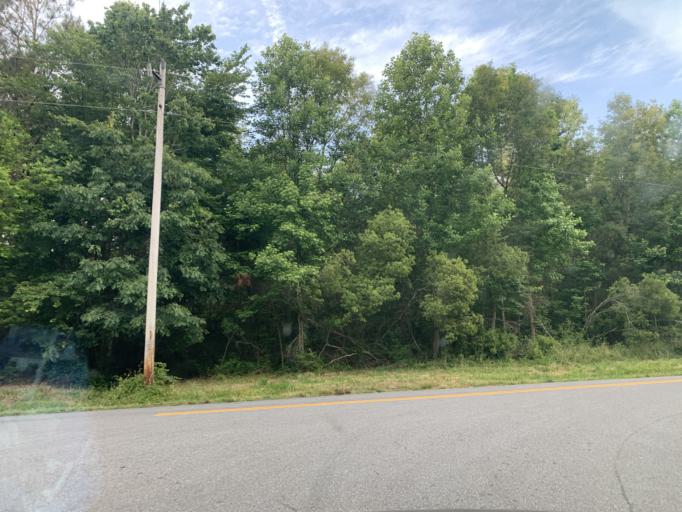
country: US
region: Maryland
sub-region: Worcester County
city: Pocomoke City
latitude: 38.0934
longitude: -75.4646
